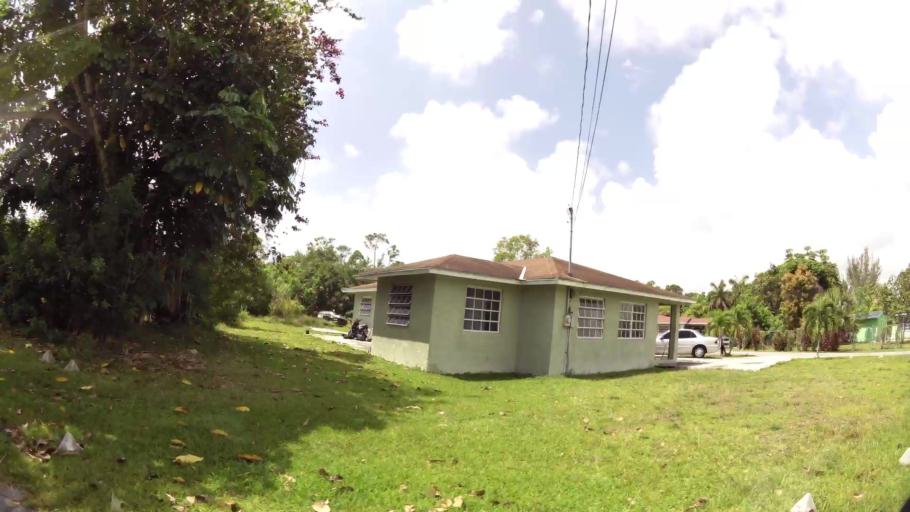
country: BS
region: Freeport
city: Lucaya
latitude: 26.5283
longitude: -78.6549
